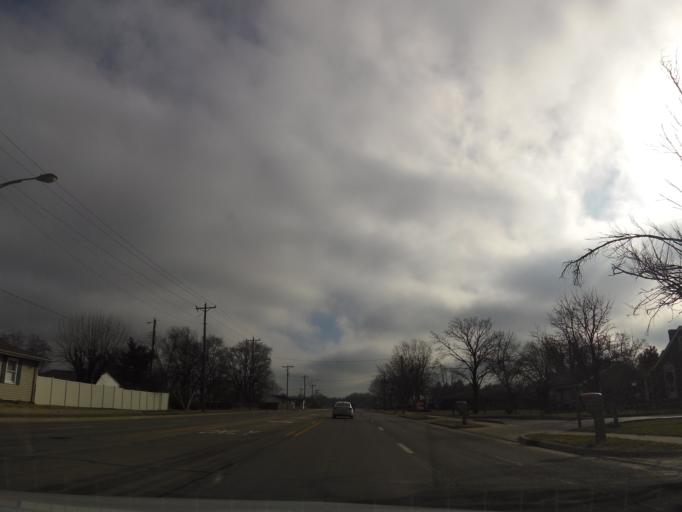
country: US
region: Indiana
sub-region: Bartholomew County
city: Columbus
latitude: 39.1923
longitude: -85.8922
